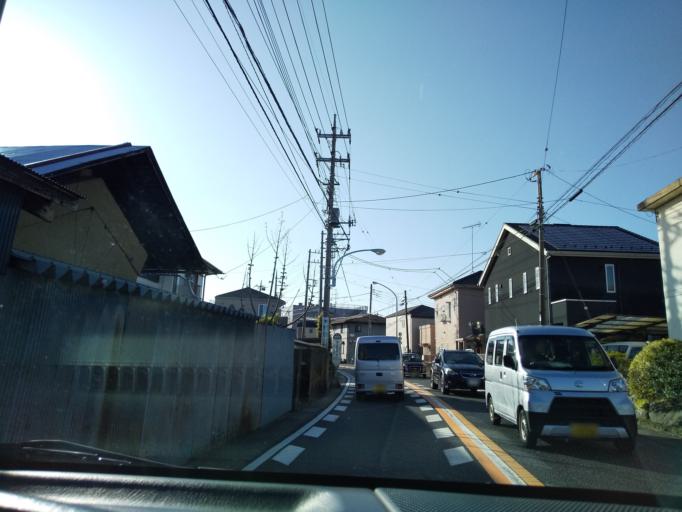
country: JP
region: Tokyo
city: Hino
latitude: 35.6938
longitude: 139.4000
